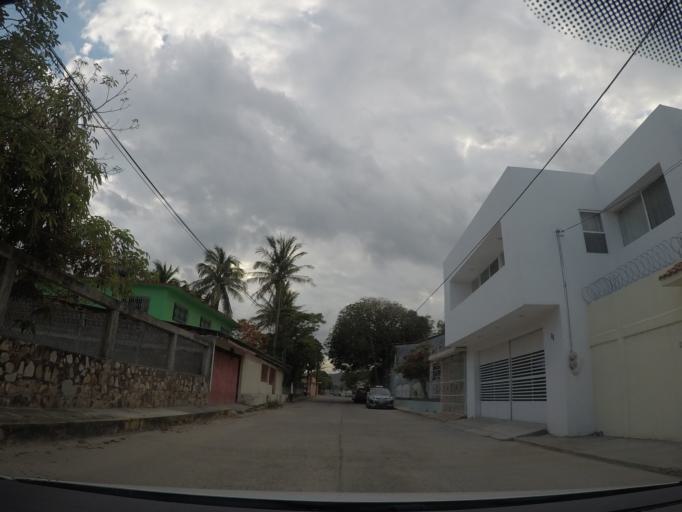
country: MX
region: Oaxaca
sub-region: Salina Cruz
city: Salina Cruz
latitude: 16.2142
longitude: -95.1959
